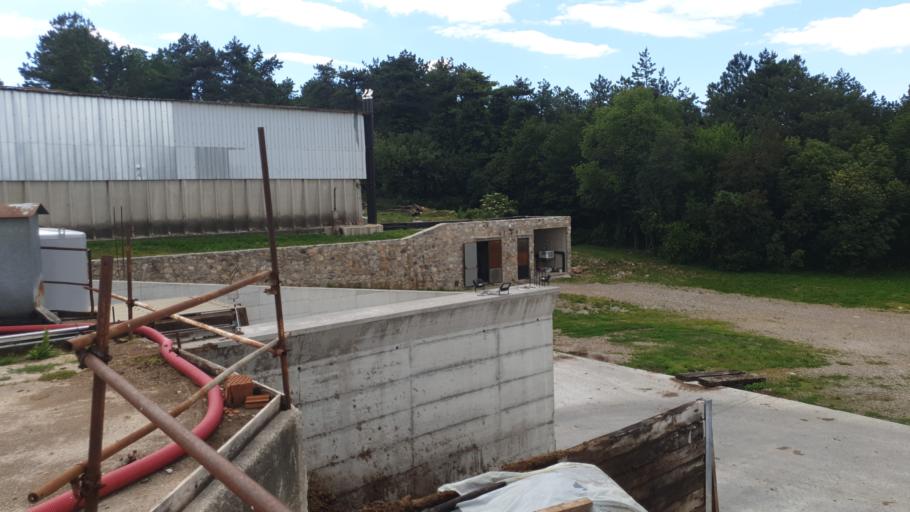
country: IT
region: Friuli Venezia Giulia
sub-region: Provincia di Trieste
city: Aurisina
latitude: 45.7680
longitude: 13.6980
